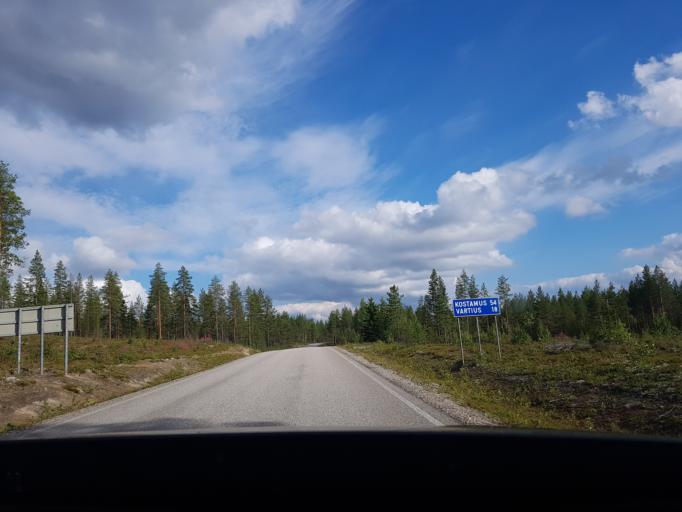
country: FI
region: Kainuu
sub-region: Kehys-Kainuu
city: Kuhmo
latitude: 64.6203
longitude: 29.7033
